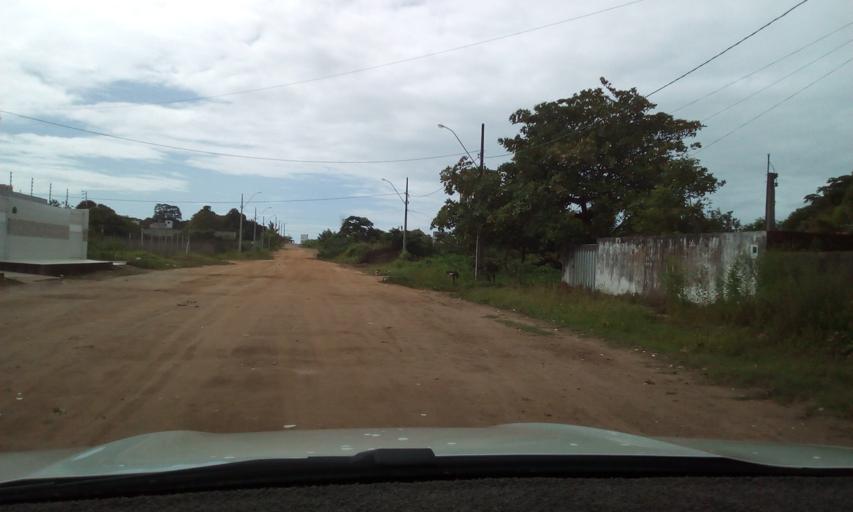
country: BR
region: Paraiba
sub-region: Joao Pessoa
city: Joao Pessoa
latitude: -7.1482
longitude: -34.8147
